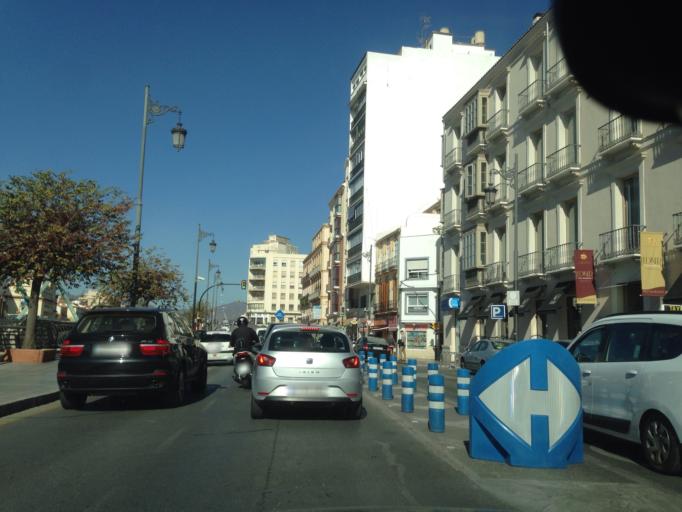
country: ES
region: Andalusia
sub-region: Provincia de Malaga
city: Malaga
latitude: 36.7202
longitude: -4.4251
